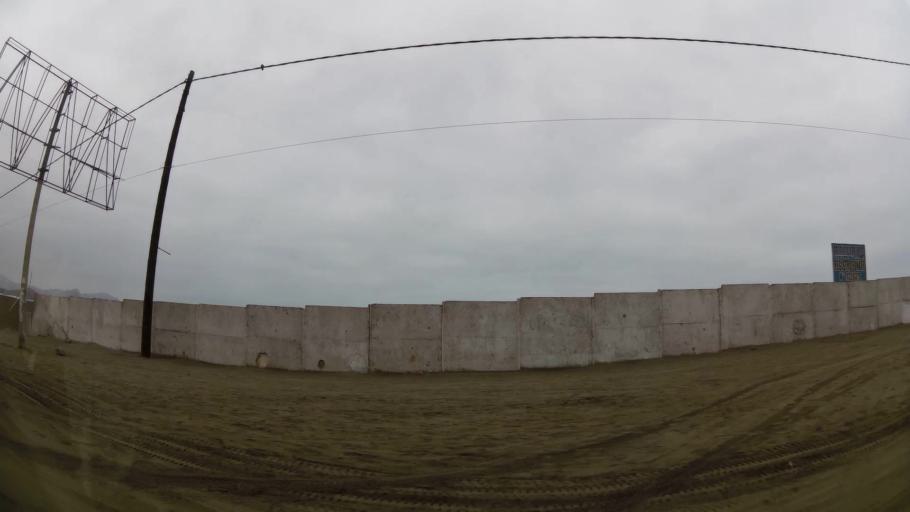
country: PE
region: Lima
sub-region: Lima
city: Punta Hermosa
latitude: -12.3550
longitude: -76.8065
